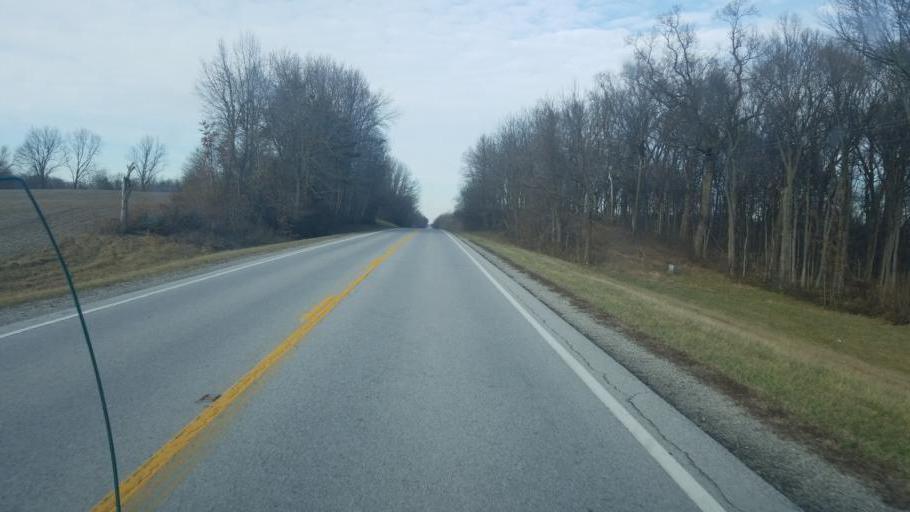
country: US
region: Illinois
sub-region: Lawrence County
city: Bridgeport
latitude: 38.5588
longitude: -87.6946
